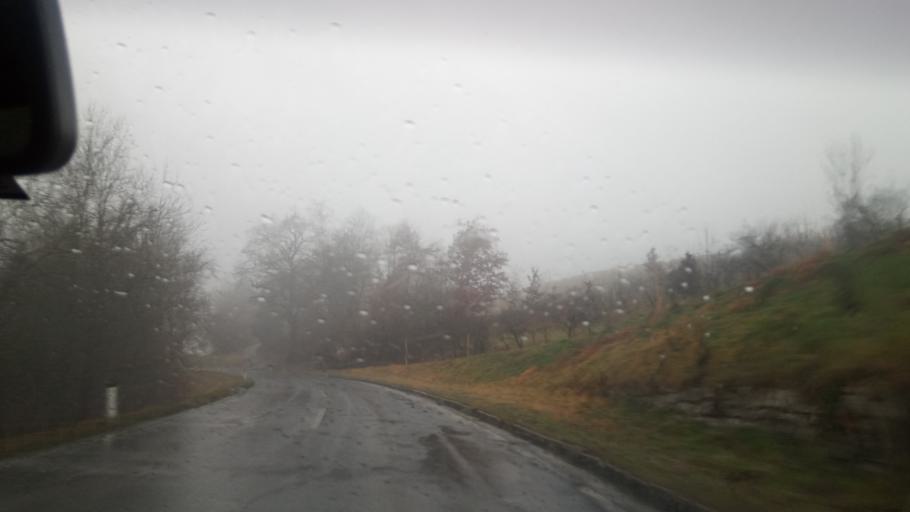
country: AT
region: Carinthia
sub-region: Politischer Bezirk Klagenfurt Land
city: Keutschach am See
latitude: 46.5899
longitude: 14.2037
